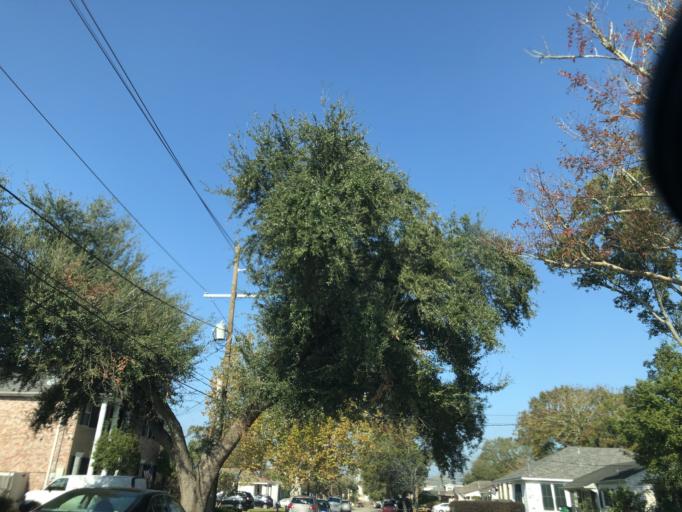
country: US
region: Louisiana
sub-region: Jefferson Parish
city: Metairie
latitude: 29.9894
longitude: -90.1525
